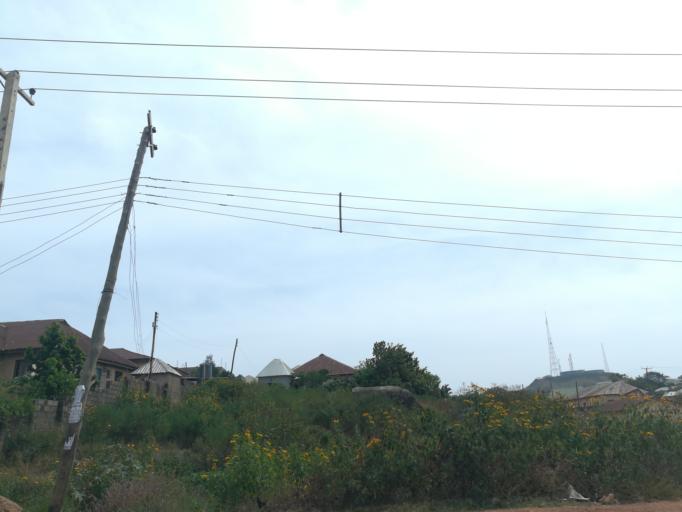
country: NG
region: Plateau
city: Jos
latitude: 9.8925
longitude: 8.8647
